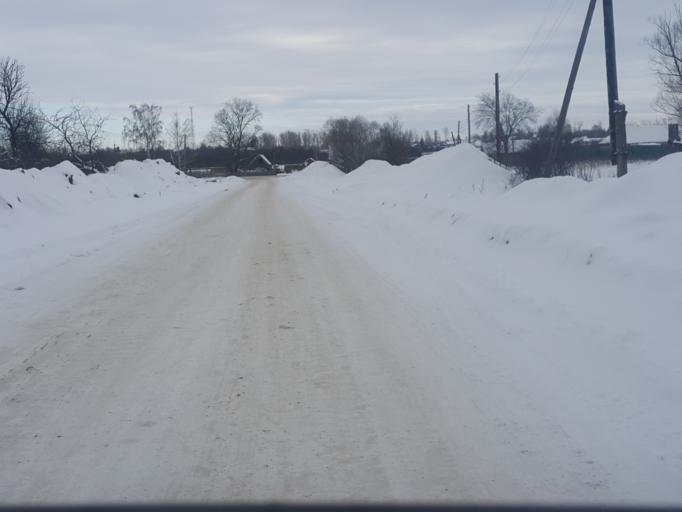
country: RU
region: Tambov
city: Platonovka
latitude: 52.8807
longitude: 41.8747
